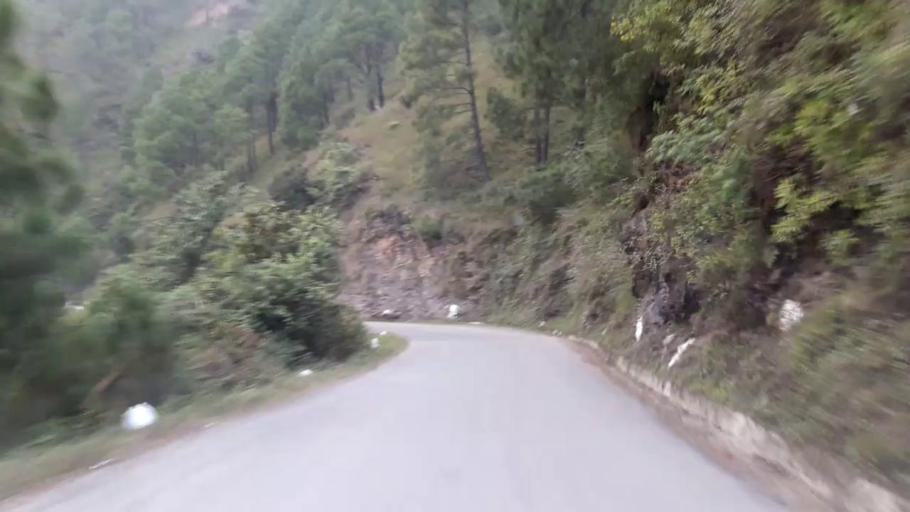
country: IN
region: Himachal Pradesh
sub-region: Shimla
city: Jutogh
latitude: 31.0490
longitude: 77.1429
